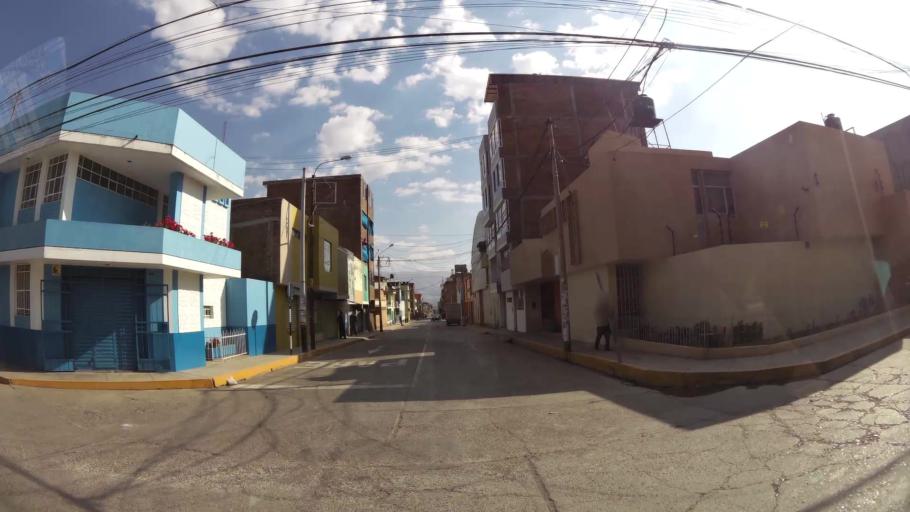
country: PE
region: Junin
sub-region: Provincia de Huancayo
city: El Tambo
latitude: -12.0613
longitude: -75.2123
